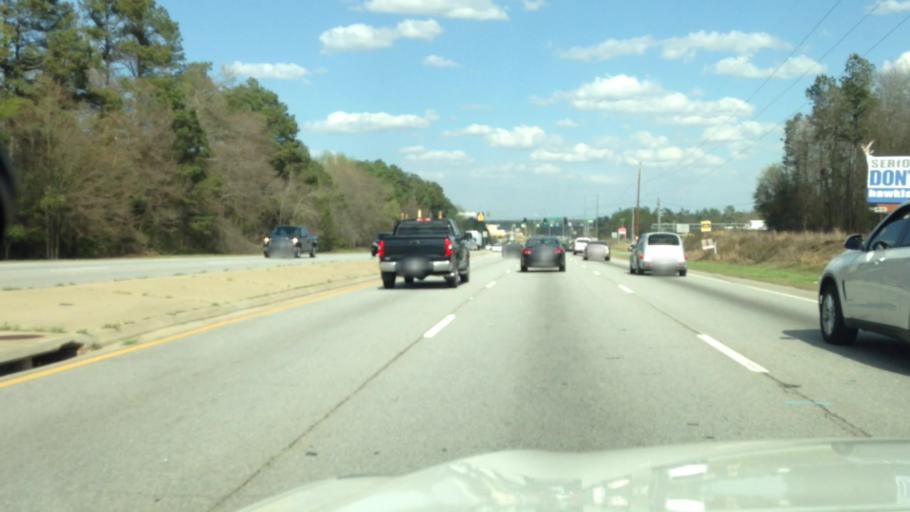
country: US
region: Georgia
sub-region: Columbia County
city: Martinez
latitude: 33.4457
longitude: -82.0904
